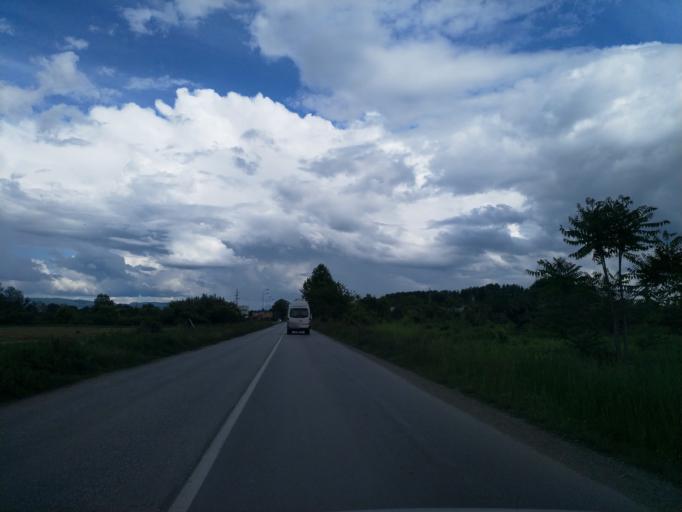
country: RS
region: Central Serbia
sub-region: Pomoravski Okrug
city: Cuprija
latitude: 43.9416
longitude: 21.3575
